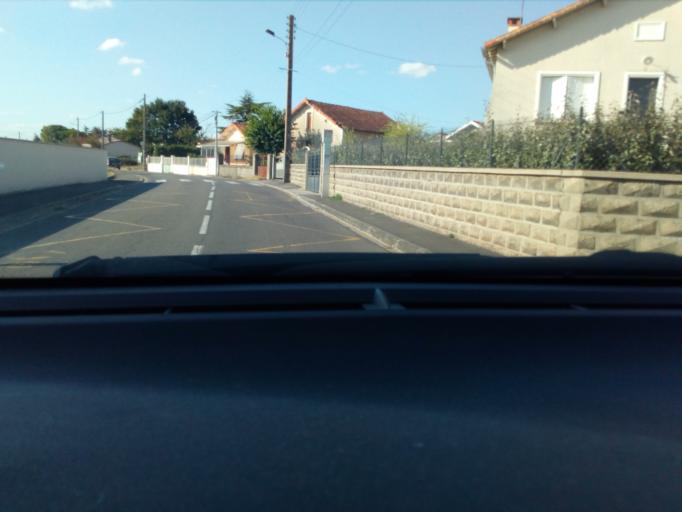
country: FR
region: Poitou-Charentes
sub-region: Departement de la Charente
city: Angouleme
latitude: 45.6633
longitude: 0.1425
